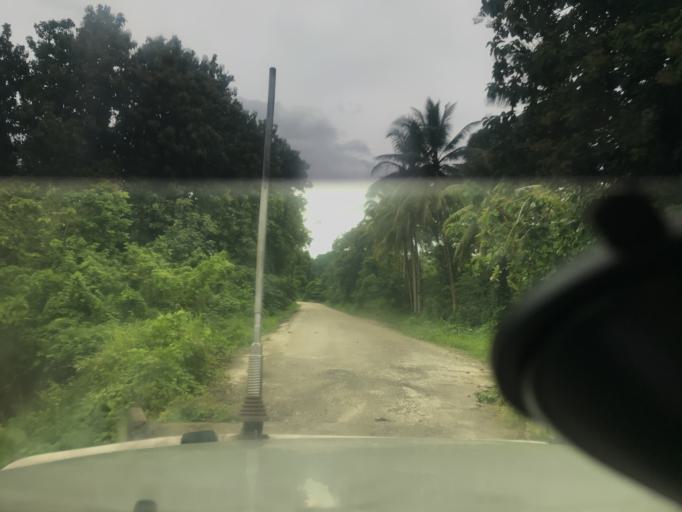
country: SB
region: Malaita
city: Auki
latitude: -8.8807
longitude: 160.7680
